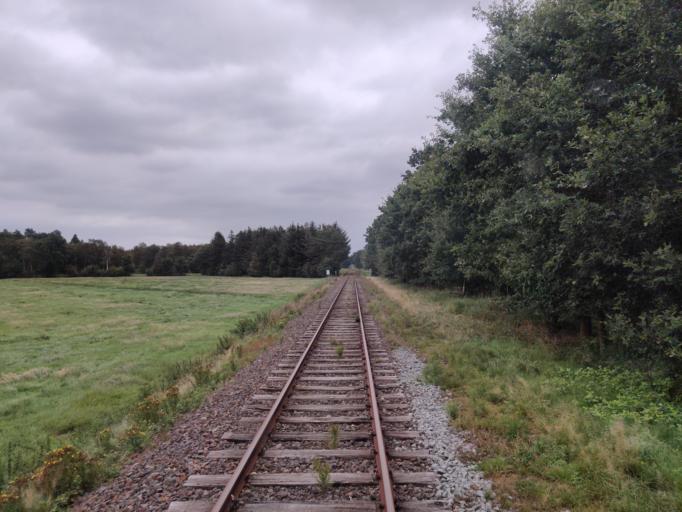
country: DE
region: Lower Saxony
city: Oerel
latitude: 53.4809
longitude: 9.0823
